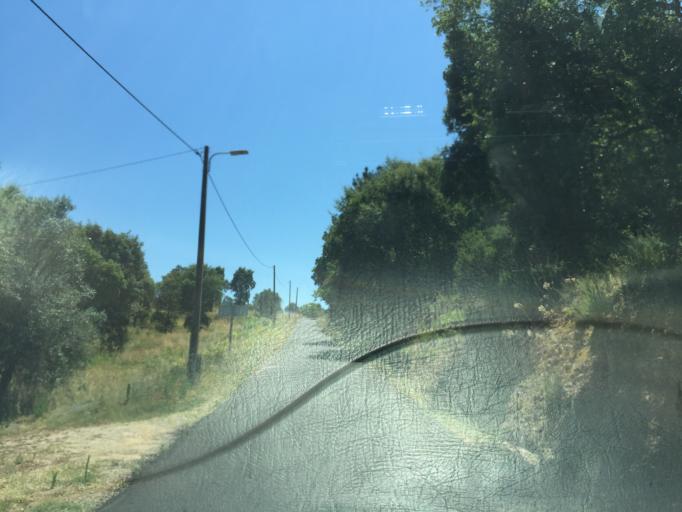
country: PT
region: Santarem
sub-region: Ferreira do Zezere
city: Ferreira do Zezere
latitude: 39.5991
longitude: -8.2732
